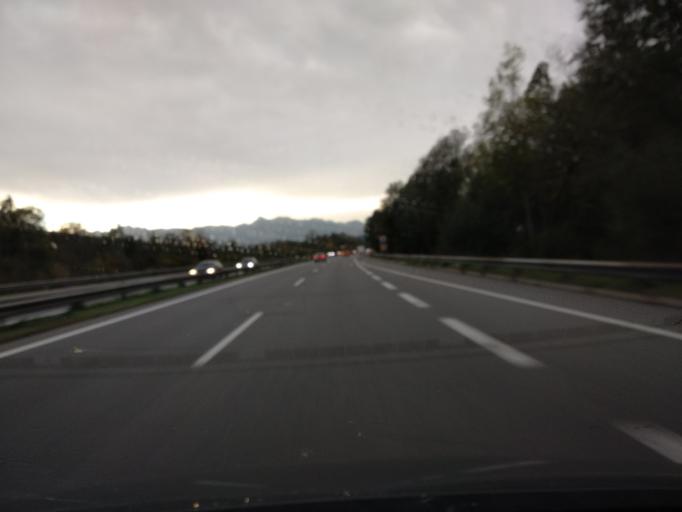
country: AT
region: Vorarlberg
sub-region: Politischer Bezirk Feldkirch
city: Satteins
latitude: 47.2031
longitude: 9.6744
